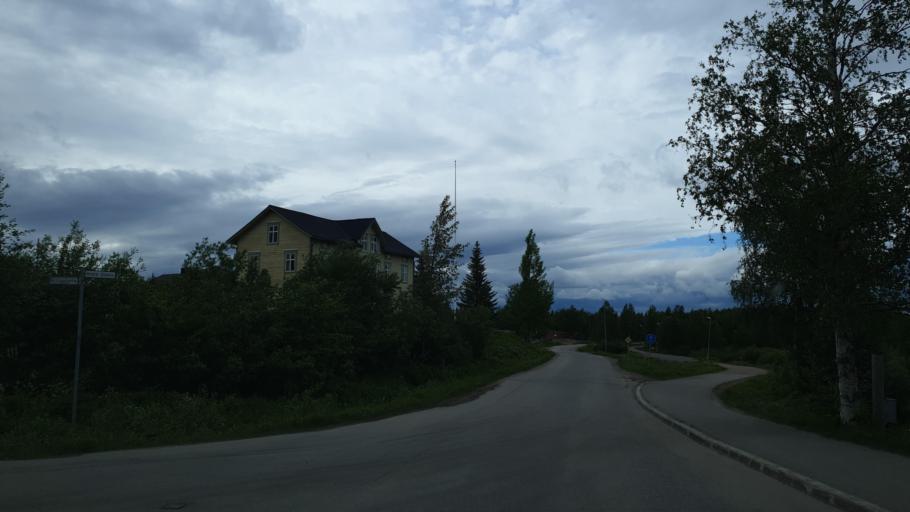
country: SE
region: Norrbotten
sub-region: Gallivare Kommun
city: Gaellivare
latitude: 67.1275
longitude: 20.6532
